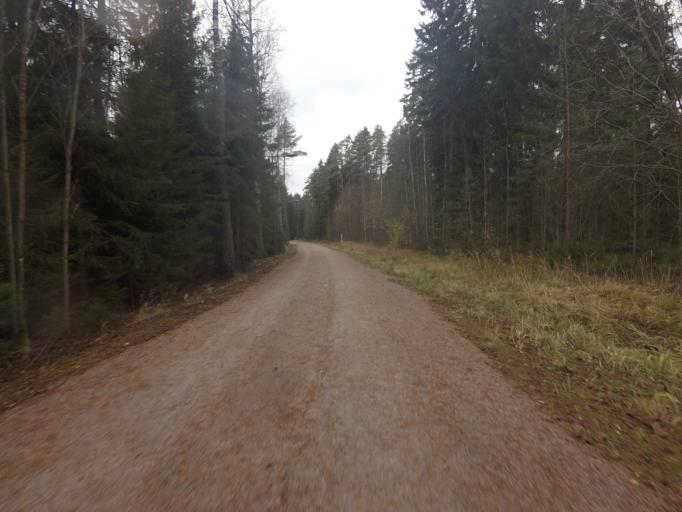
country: FI
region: Uusimaa
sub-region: Helsinki
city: Kauniainen
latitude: 60.1833
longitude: 24.7014
